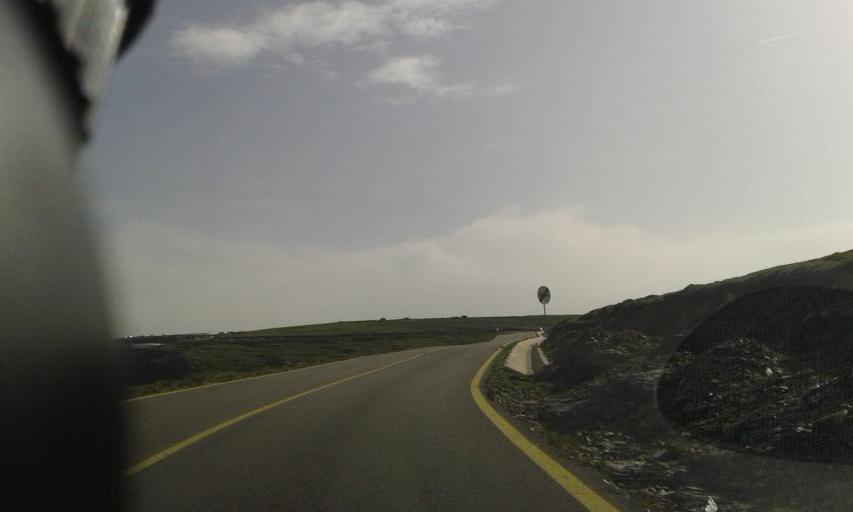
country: RO
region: Gorj
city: Novaci-Straini
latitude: 45.3707
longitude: 23.6533
